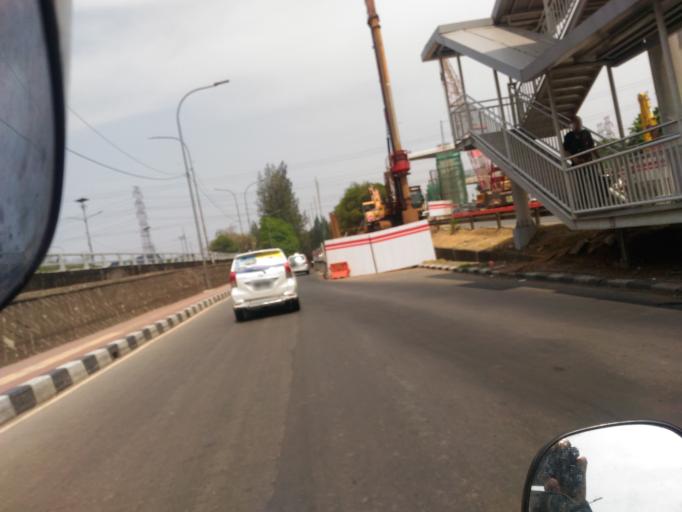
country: ID
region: Jakarta Raya
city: Jakarta
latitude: -6.2462
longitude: 106.8732
